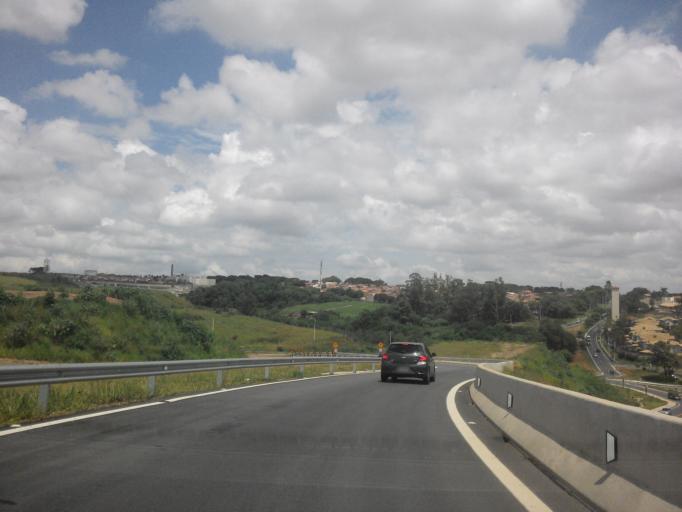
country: BR
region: Sao Paulo
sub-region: Campinas
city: Campinas
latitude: -22.8665
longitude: -47.0209
